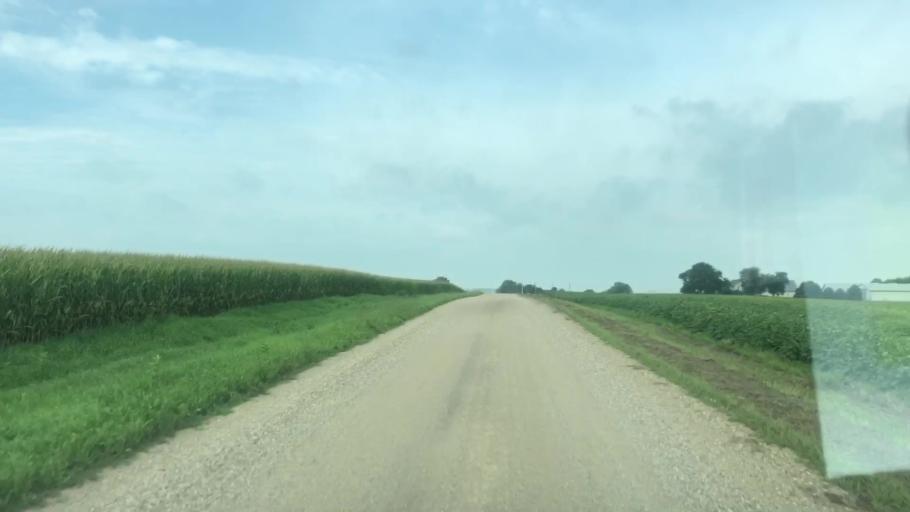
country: US
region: Iowa
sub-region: Lyon County
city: George
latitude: 43.2726
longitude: -95.9957
